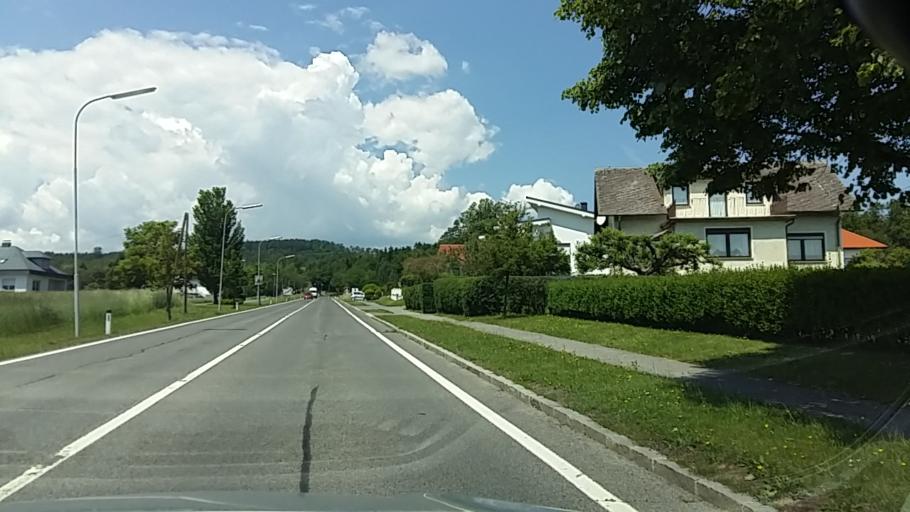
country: AT
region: Burgenland
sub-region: Politischer Bezirk Oberwart
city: Unterkohlstatten
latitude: 47.3965
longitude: 16.3204
